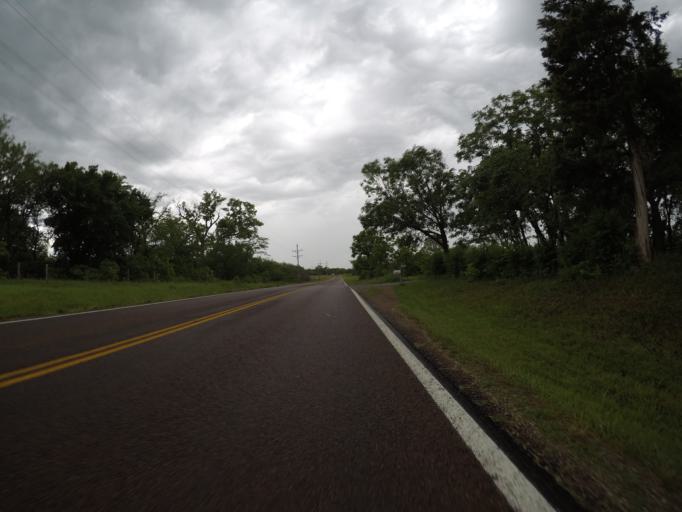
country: US
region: Kansas
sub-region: Shawnee County
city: Rossville
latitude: 38.9573
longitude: -96.0691
